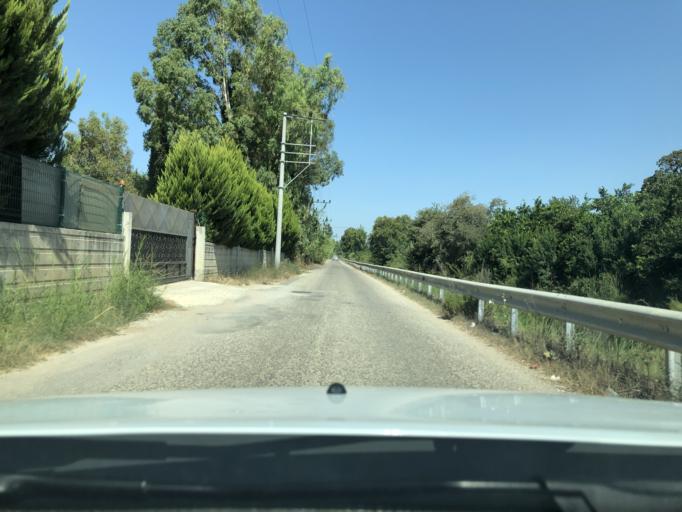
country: TR
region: Antalya
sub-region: Manavgat
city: Manavgat
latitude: 36.8030
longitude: 31.4685
